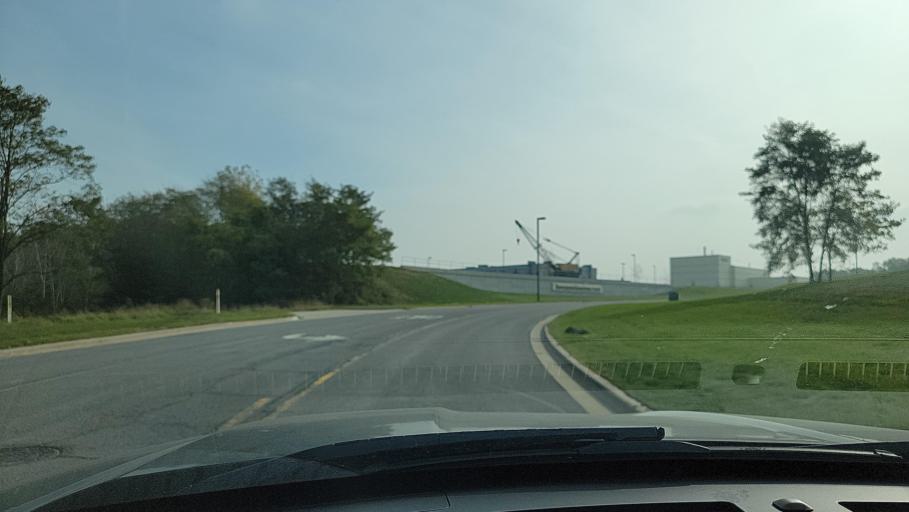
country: US
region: Indiana
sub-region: Porter County
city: Burns Harbor
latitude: 41.6087
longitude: -87.1570
